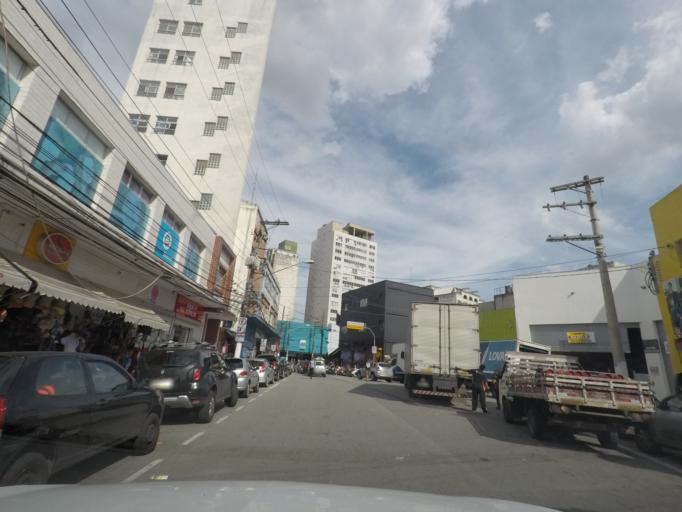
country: BR
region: Sao Paulo
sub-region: Taboao Da Serra
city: Taboao da Serra
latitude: -23.6518
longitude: -46.7060
